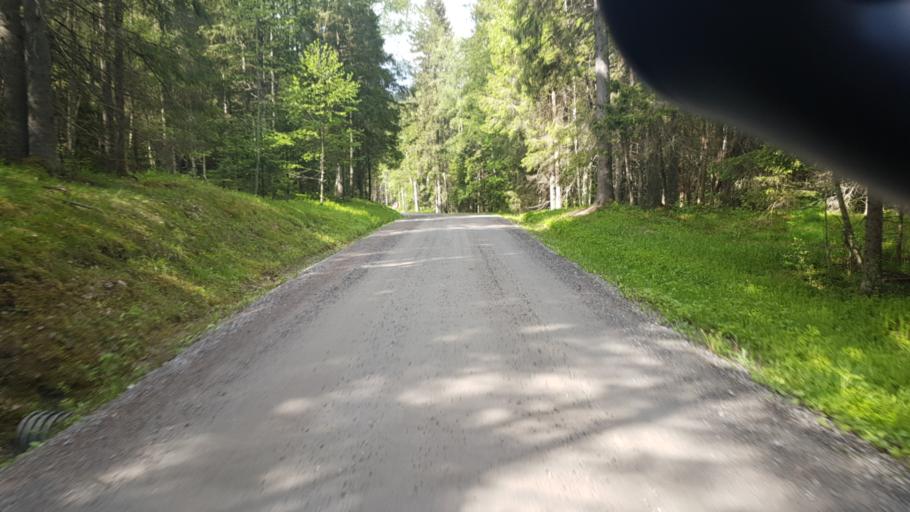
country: NO
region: Ostfold
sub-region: Romskog
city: Romskog
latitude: 59.7016
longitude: 11.9498
